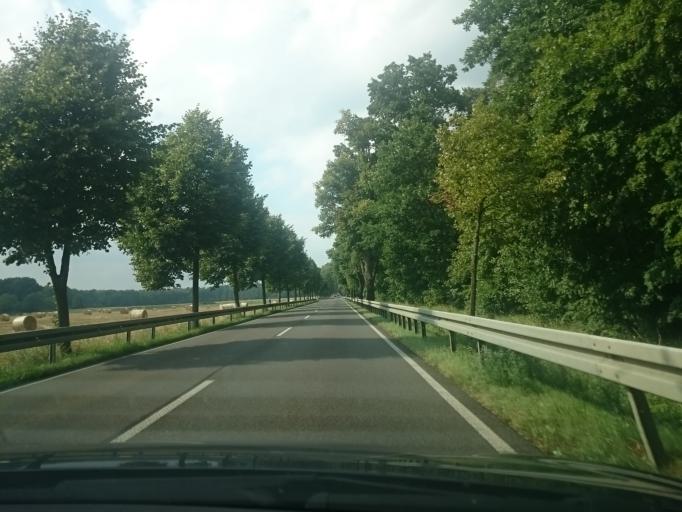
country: DE
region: Mecklenburg-Vorpommern
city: Ducherow
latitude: 53.7256
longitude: 13.8151
